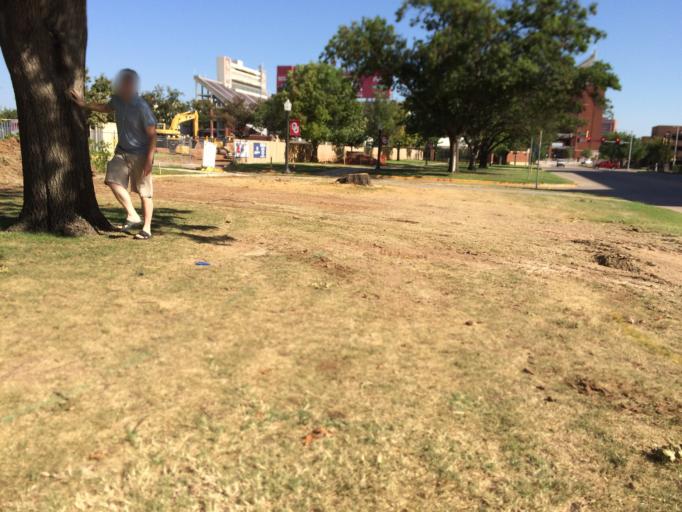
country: US
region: Oklahoma
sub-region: Cleveland County
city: Norman
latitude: 35.2026
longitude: -97.4414
